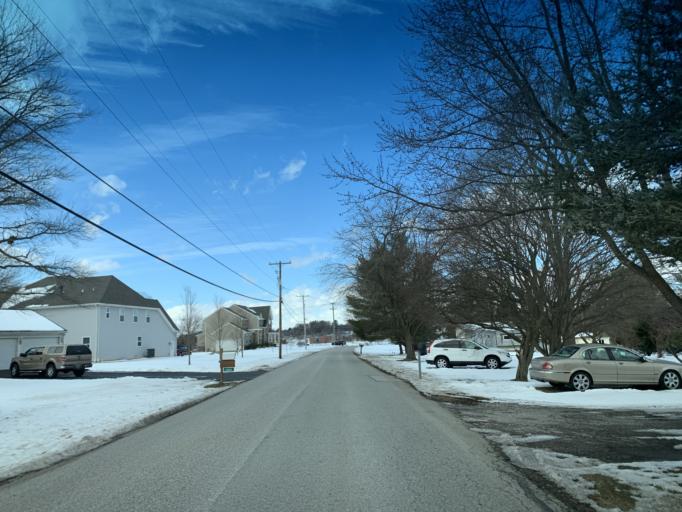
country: US
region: Pennsylvania
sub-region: York County
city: Shrewsbury
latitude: 39.7574
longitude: -76.6699
